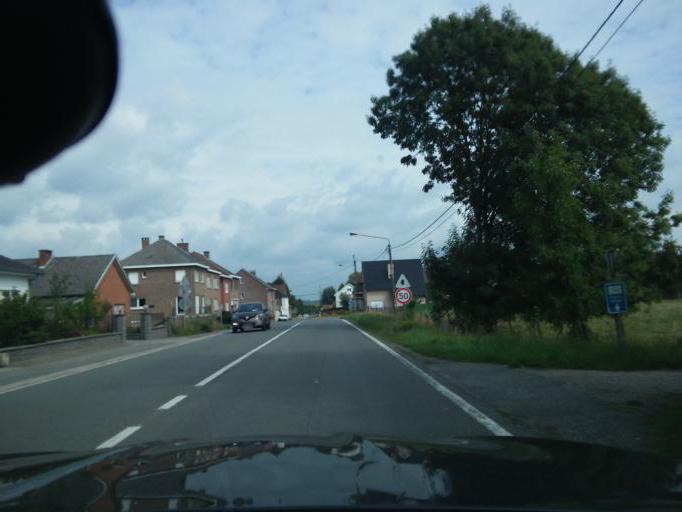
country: BE
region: Wallonia
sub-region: Province du Hainaut
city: Enghien
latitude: 50.6897
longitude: 4.0555
